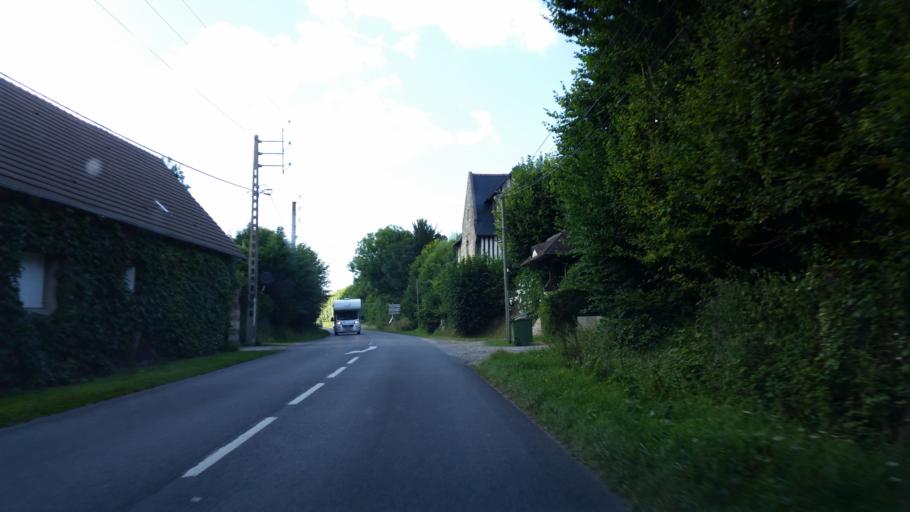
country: FR
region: Lower Normandy
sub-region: Departement du Calvados
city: Touques
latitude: 49.3363
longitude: 0.1102
